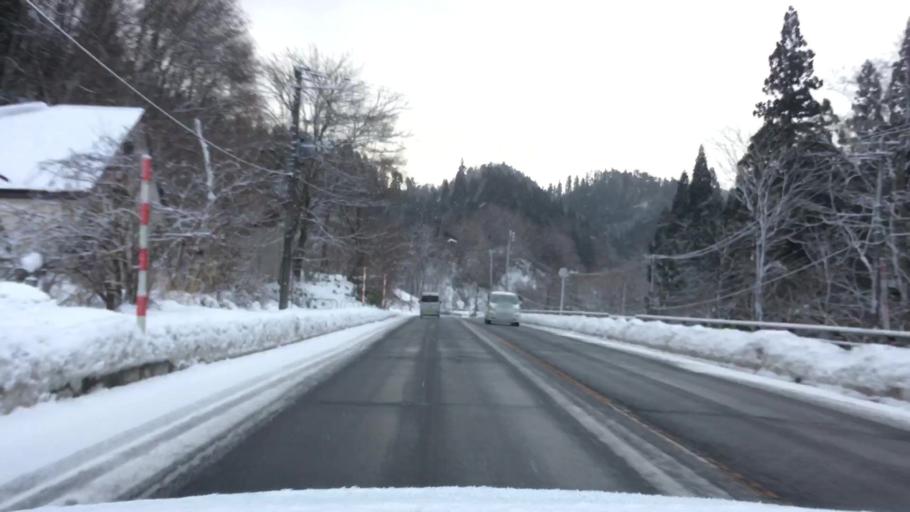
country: JP
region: Akita
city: Odate
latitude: 40.4315
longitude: 140.6364
